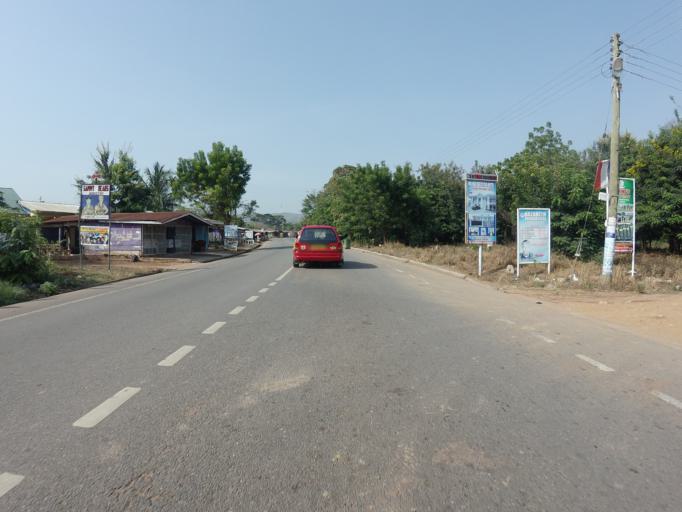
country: GH
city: Akropong
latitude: 6.1177
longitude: -0.0036
